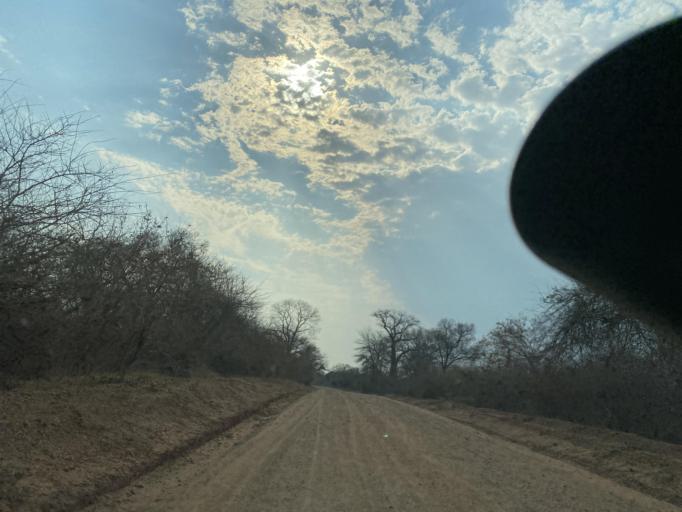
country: ZW
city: Chirundu
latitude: -15.9312
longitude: 28.9256
